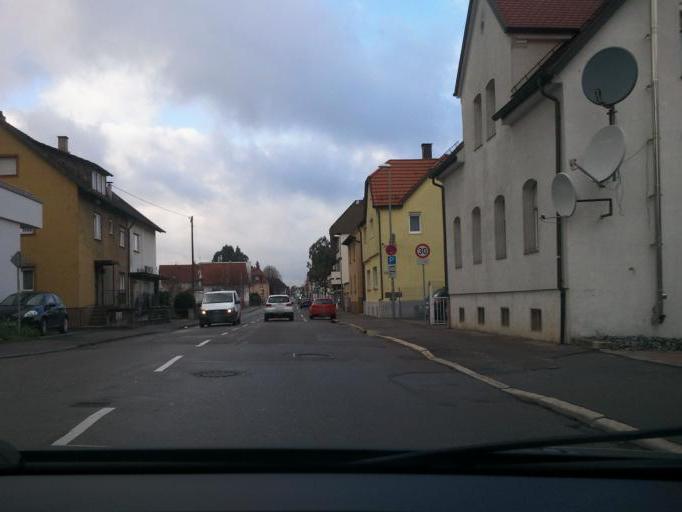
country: DE
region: Baden-Wuerttemberg
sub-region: Regierungsbezirk Stuttgart
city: Asperg
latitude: 48.9043
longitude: 9.1400
